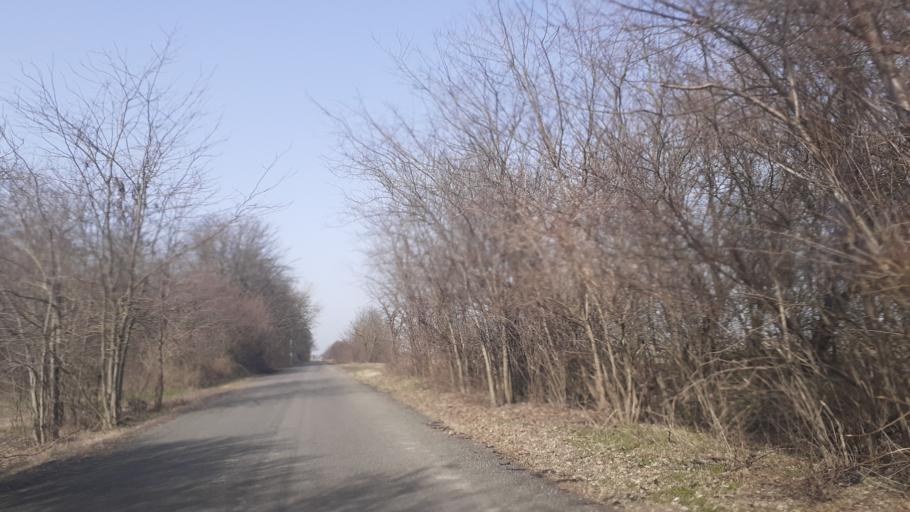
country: HU
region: Pest
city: Dabas
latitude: 47.1216
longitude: 19.2127
